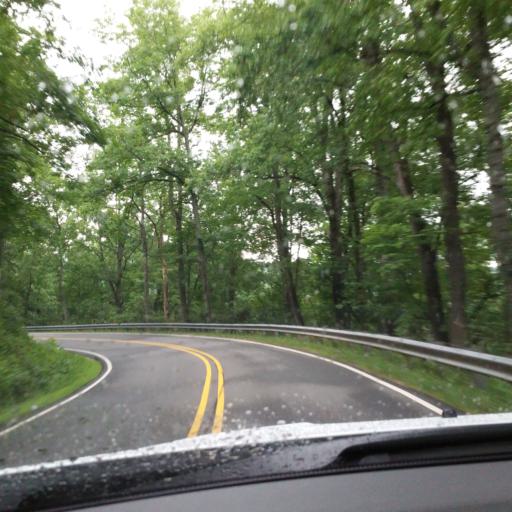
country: US
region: North Carolina
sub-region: Mitchell County
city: Spruce Pine
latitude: 35.7726
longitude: -82.1752
